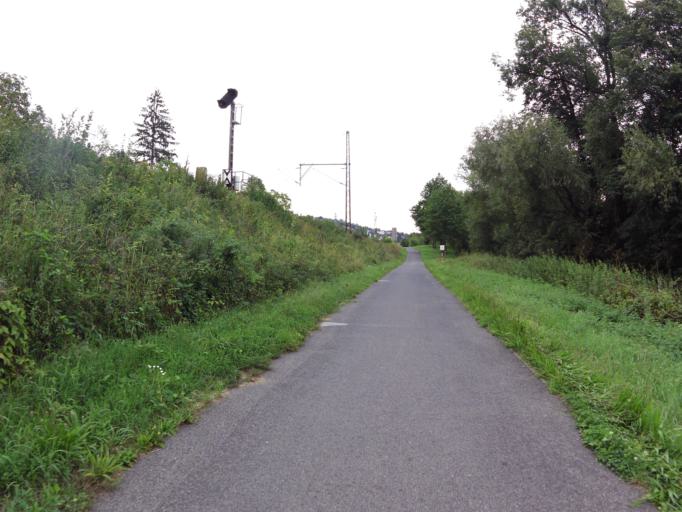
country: DE
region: Bavaria
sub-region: Regierungsbezirk Unterfranken
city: Schonungen
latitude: 50.0524
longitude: 10.2980
